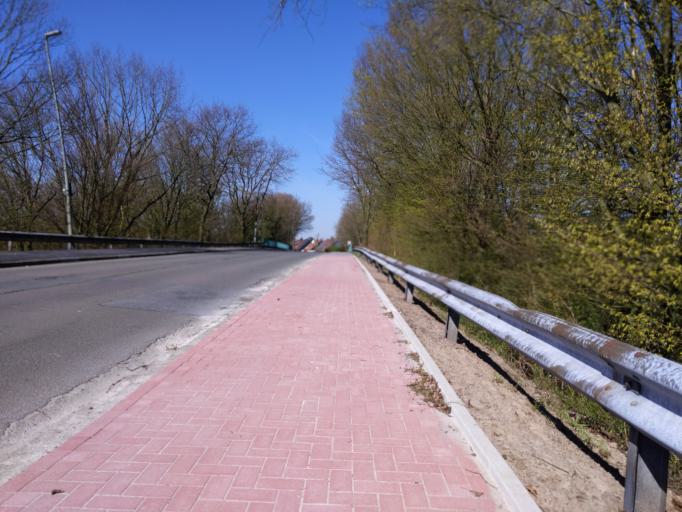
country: DE
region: North Rhine-Westphalia
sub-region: Regierungsbezirk Dusseldorf
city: Schermbeck
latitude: 51.6872
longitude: 6.8806
